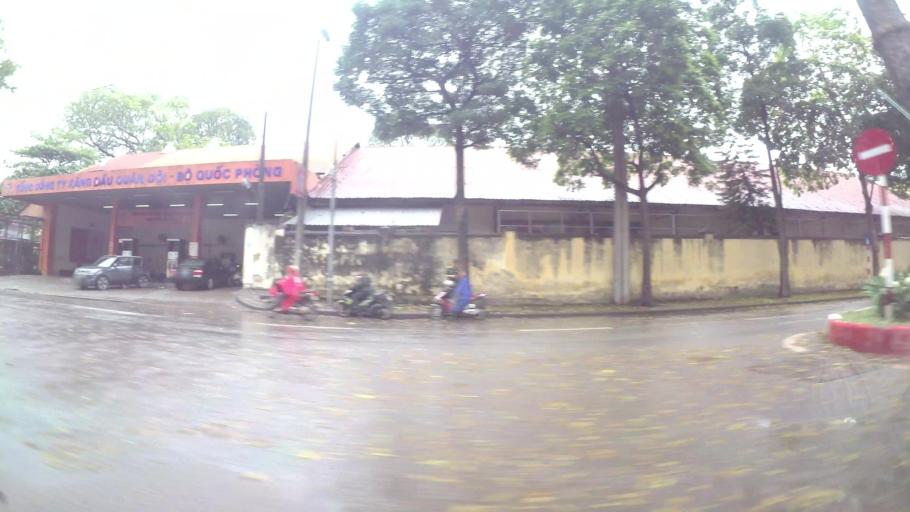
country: VN
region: Ha Noi
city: Hoan Kiem
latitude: 21.0395
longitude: 105.8418
